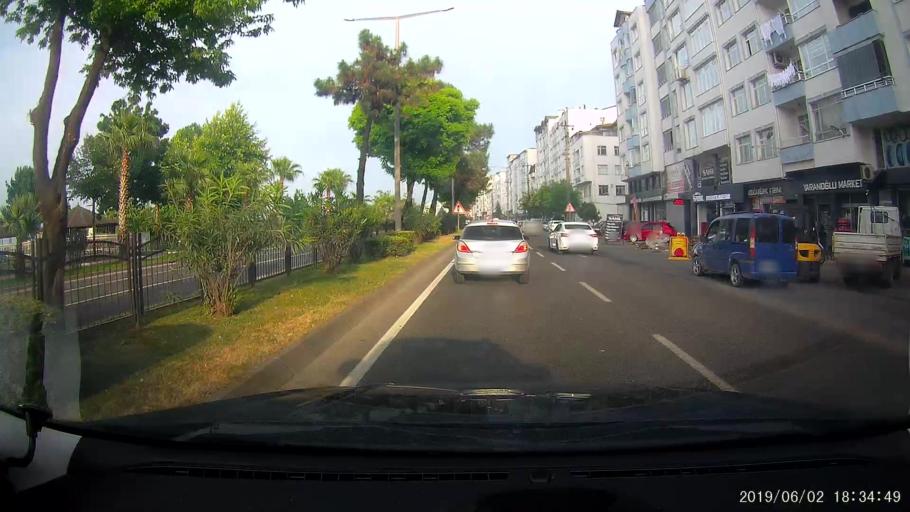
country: TR
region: Ordu
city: Fatsa
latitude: 41.0280
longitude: 37.5083
